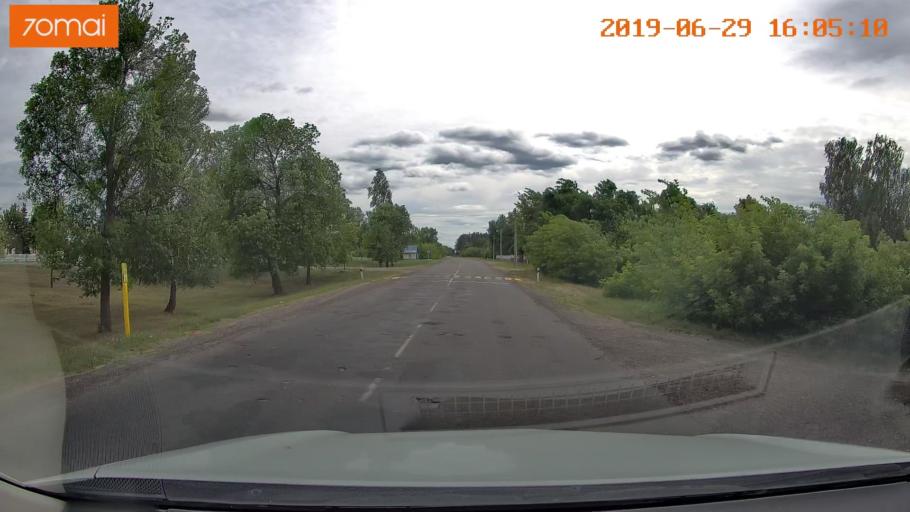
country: BY
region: Brest
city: Luninyets
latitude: 52.2179
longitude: 27.0206
